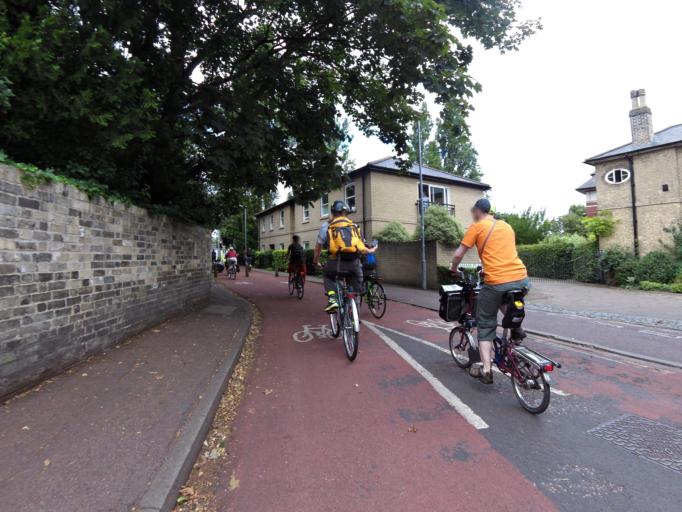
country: GB
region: England
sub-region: Cambridgeshire
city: Cambridge
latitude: 52.2001
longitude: 0.1295
